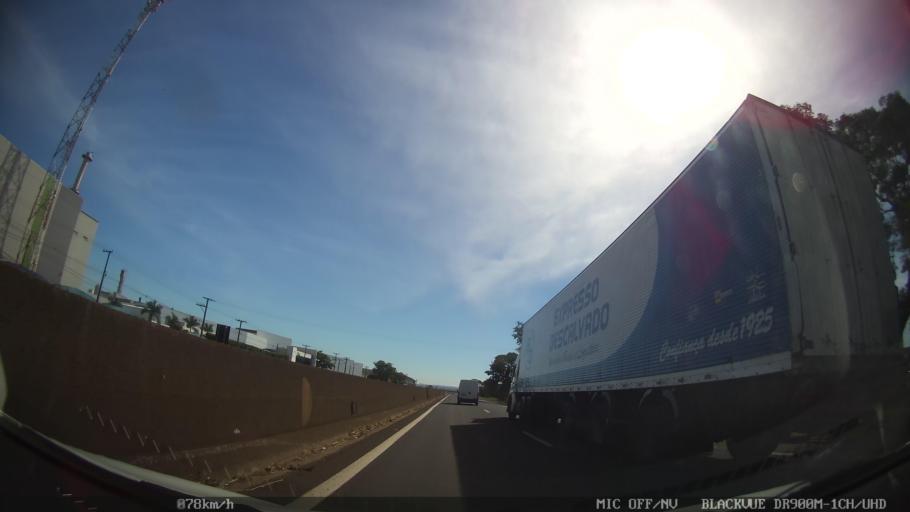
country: BR
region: Sao Paulo
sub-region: Porto Ferreira
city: Porto Ferreira
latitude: -21.8577
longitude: -47.4936
